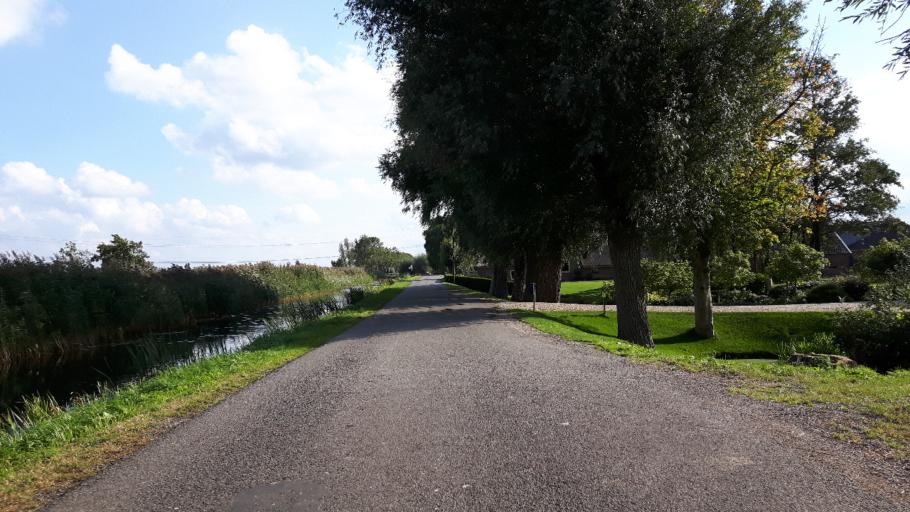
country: NL
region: Utrecht
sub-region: Stichtse Vecht
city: Breukelen
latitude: 52.1357
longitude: 4.9590
